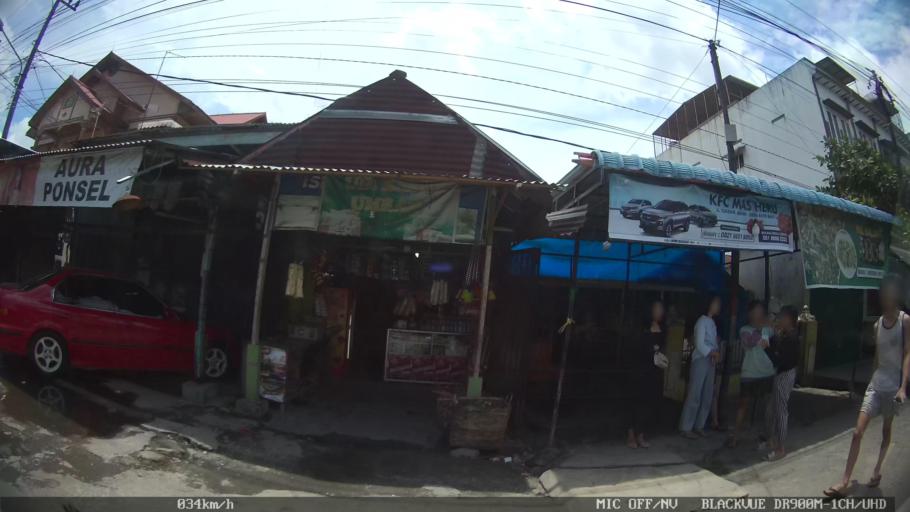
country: ID
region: North Sumatra
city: Medan
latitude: 3.6155
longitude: 98.7061
